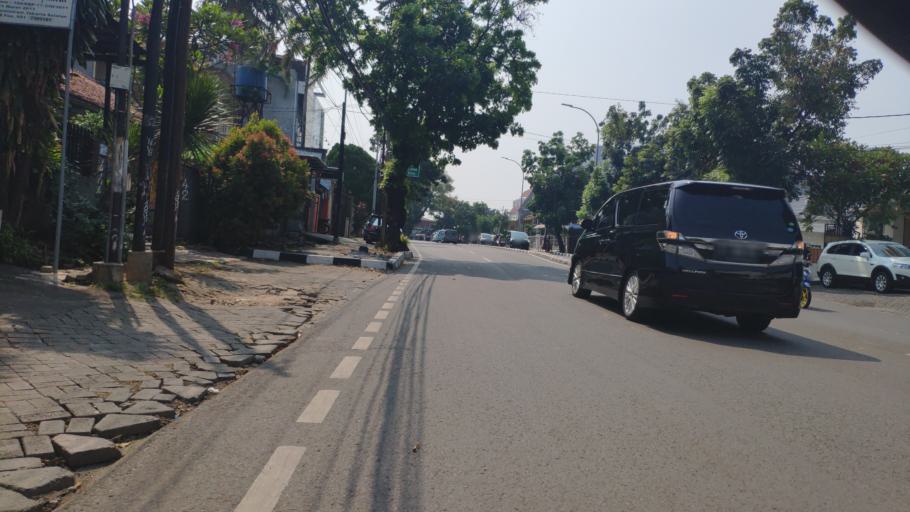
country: ID
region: Jakarta Raya
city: Jakarta
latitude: -6.2496
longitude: 106.7927
